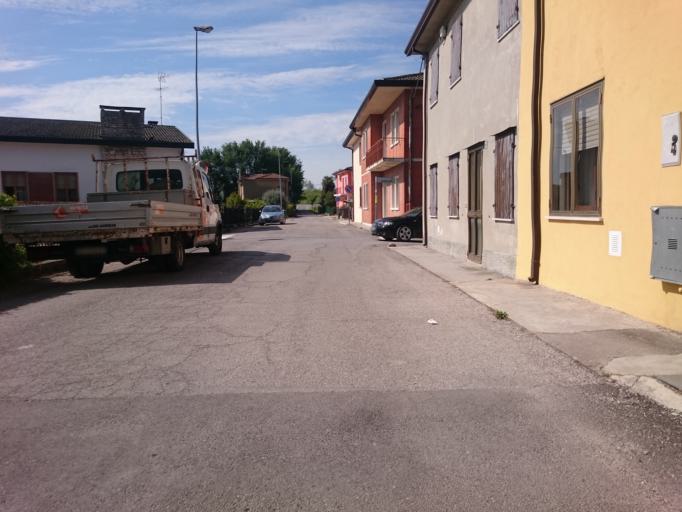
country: IT
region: Veneto
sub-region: Provincia di Rovigo
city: Corbola
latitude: 45.0043
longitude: 12.0769
